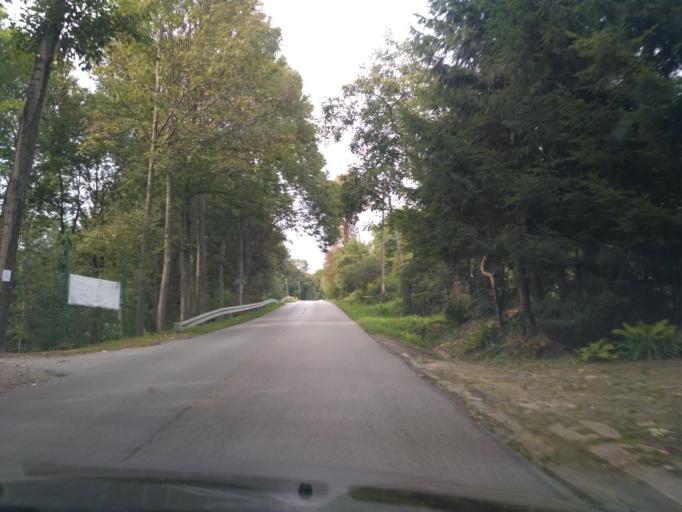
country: PL
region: Subcarpathian Voivodeship
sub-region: Powiat rzeszowski
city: Trzciana
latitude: 50.0464
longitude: 21.8327
